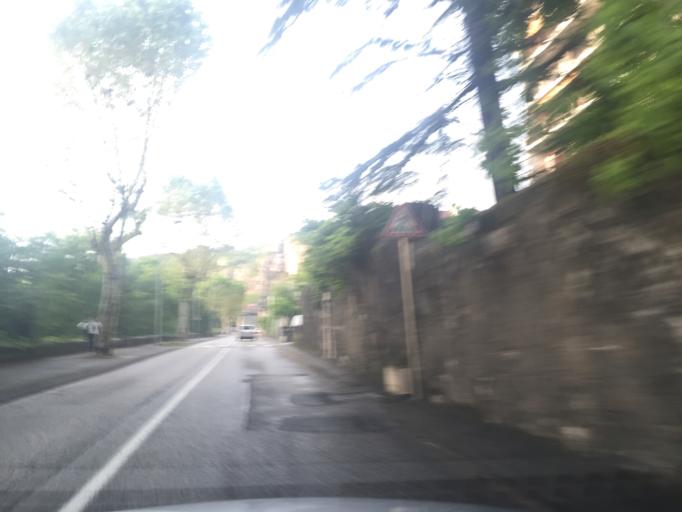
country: FR
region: Rhone-Alpes
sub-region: Departement de la Savoie
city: Chambery
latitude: 45.5759
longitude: 5.9238
